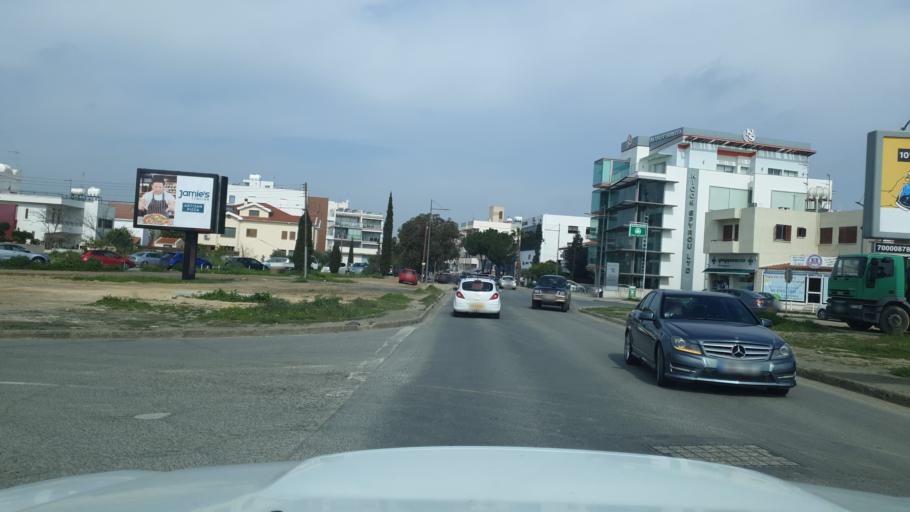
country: CY
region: Lefkosia
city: Nicosia
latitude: 35.1538
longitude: 33.3170
